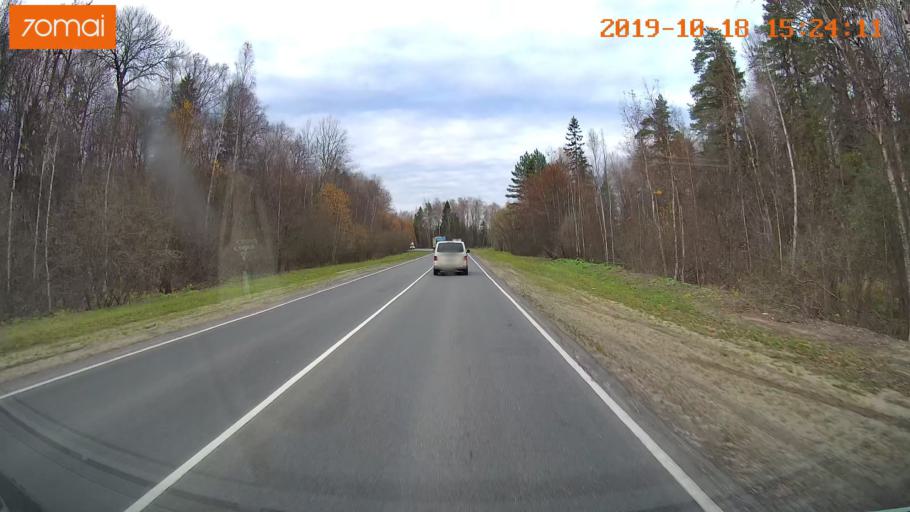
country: RU
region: Vladimir
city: Anopino
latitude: 55.7313
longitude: 40.7250
